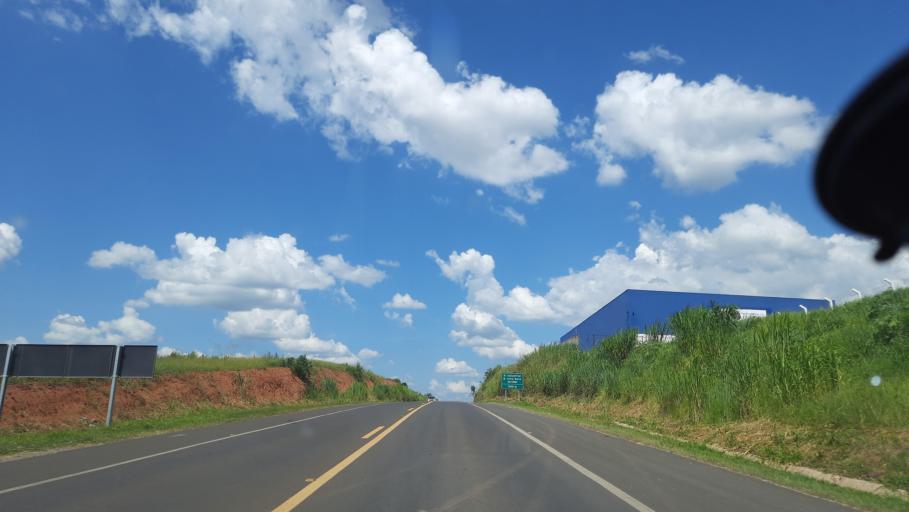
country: BR
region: Sao Paulo
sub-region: Sao Jose Do Rio Pardo
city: Sao Jose do Rio Pardo
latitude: -21.6033
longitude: -46.9218
